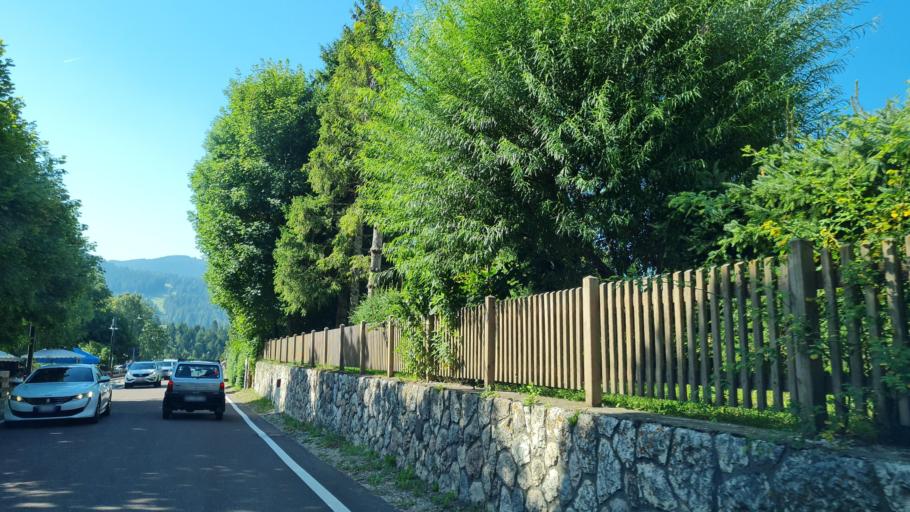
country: IT
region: Trentino-Alto Adige
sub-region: Provincia di Trento
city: Folgaria
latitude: 45.9177
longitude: 11.1862
